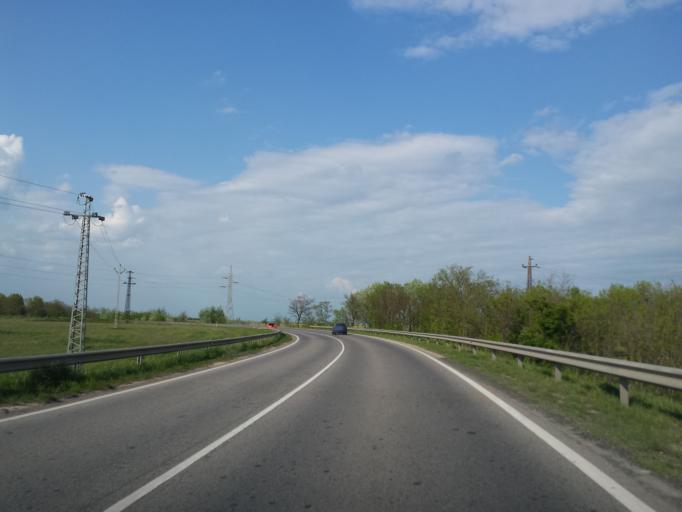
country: HU
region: Csongrad
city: Mako
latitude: 46.2494
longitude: 20.4844
